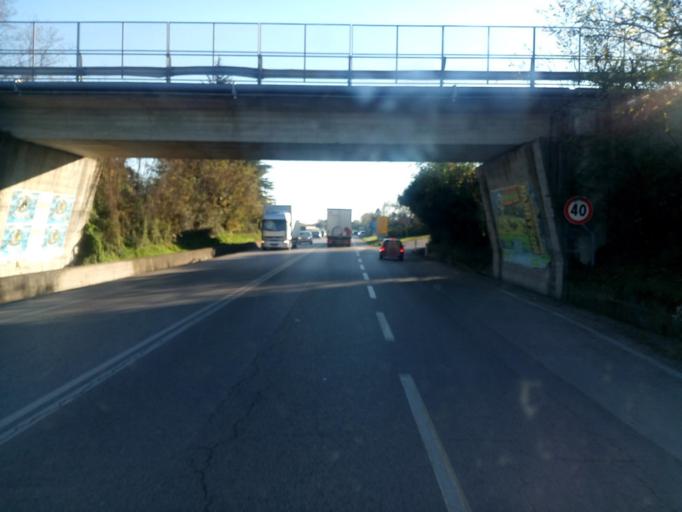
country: IT
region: Veneto
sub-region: Provincia di Vicenza
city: Bassano del Grappa
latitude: 45.7381
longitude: 11.7311
